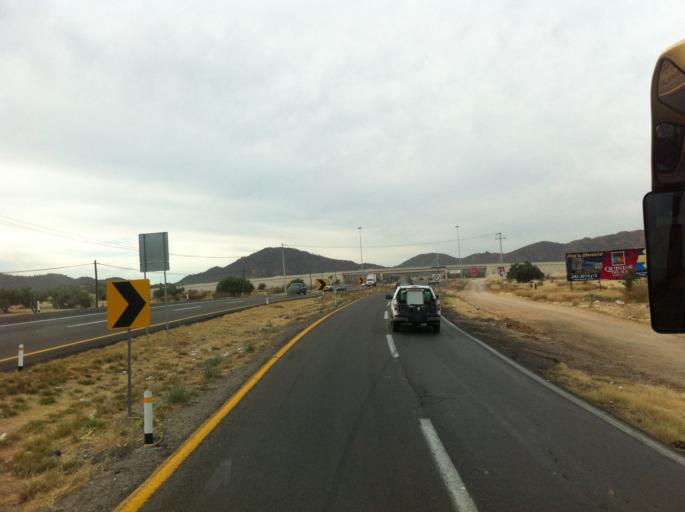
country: MX
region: Sonora
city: Hermosillo
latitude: 29.0133
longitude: -110.9624
